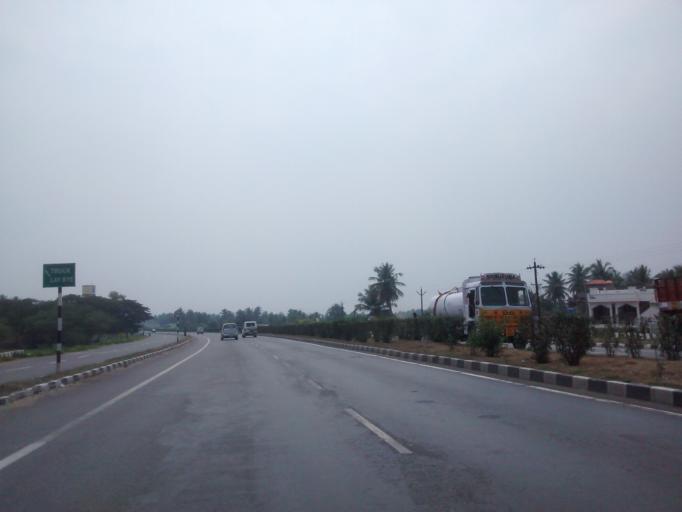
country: IN
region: Tamil Nadu
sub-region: Krishnagiri
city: Kaverippattanam
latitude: 12.4570
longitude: 78.2157
